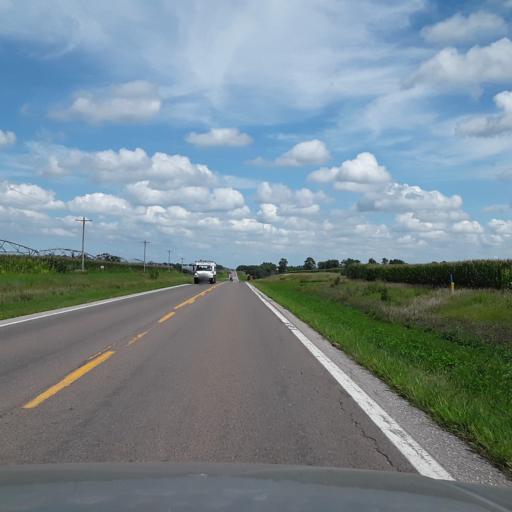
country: US
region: Nebraska
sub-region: Polk County
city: Osceola
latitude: 41.0863
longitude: -97.4257
